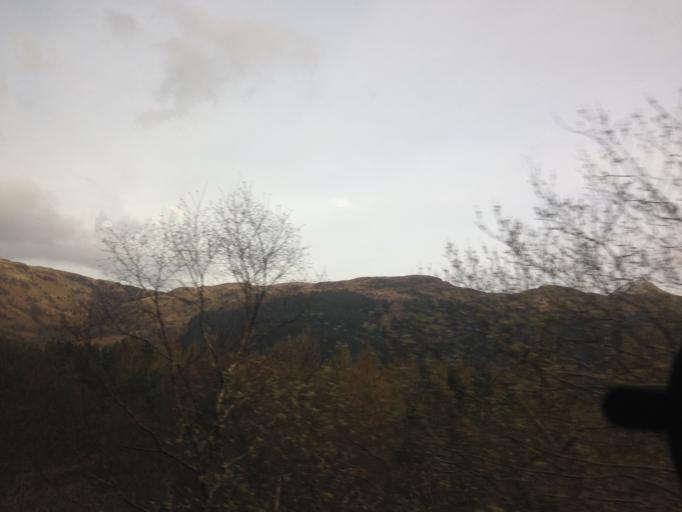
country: GB
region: Scotland
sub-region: Argyll and Bute
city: Garelochhead
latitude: 56.2140
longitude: -4.6999
